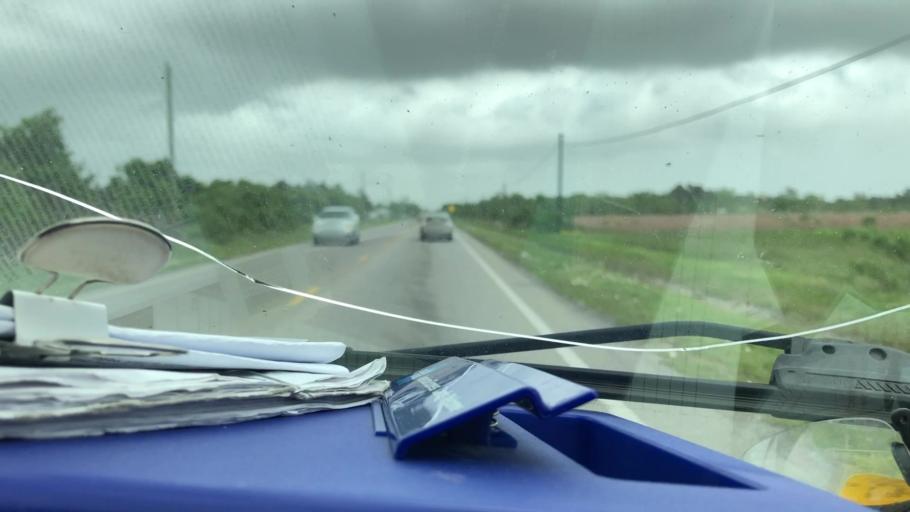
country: US
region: Texas
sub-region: Galveston County
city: Bacliff
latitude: 29.4775
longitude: -94.9709
